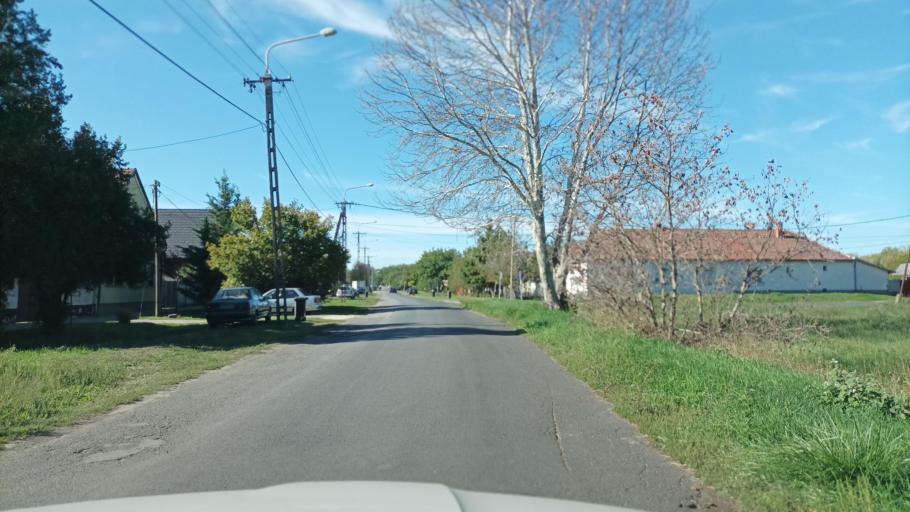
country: HU
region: Pest
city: Cegledbercel
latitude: 47.2188
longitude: 19.6616
